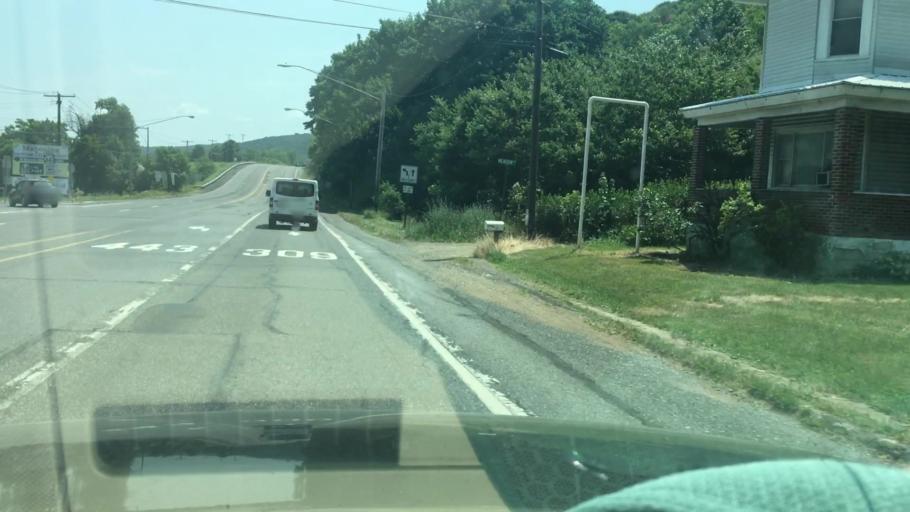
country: US
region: Pennsylvania
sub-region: Schuylkill County
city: Tamaqua
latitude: 40.7554
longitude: -75.9274
